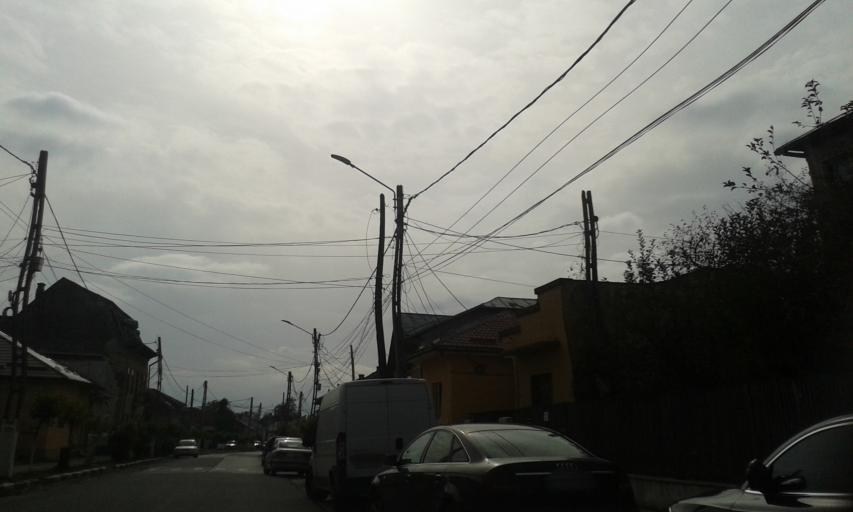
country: RO
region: Gorj
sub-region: Comuna Targu Carbunesti
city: Targu Carbunesti
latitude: 44.9541
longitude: 23.5140
